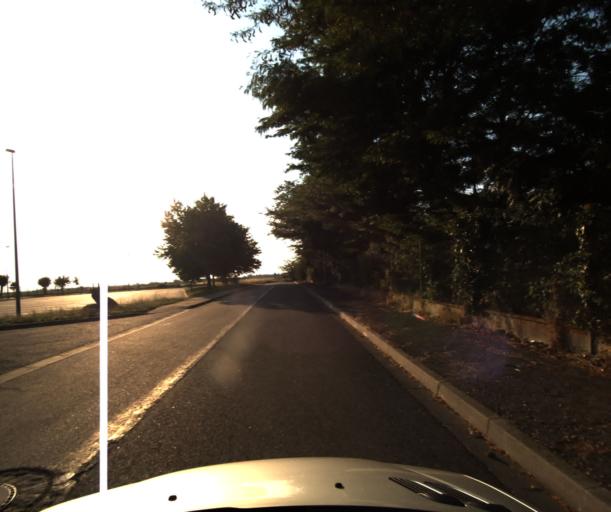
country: FR
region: Midi-Pyrenees
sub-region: Departement de la Haute-Garonne
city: Roquettes
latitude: 43.4847
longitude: 1.3870
